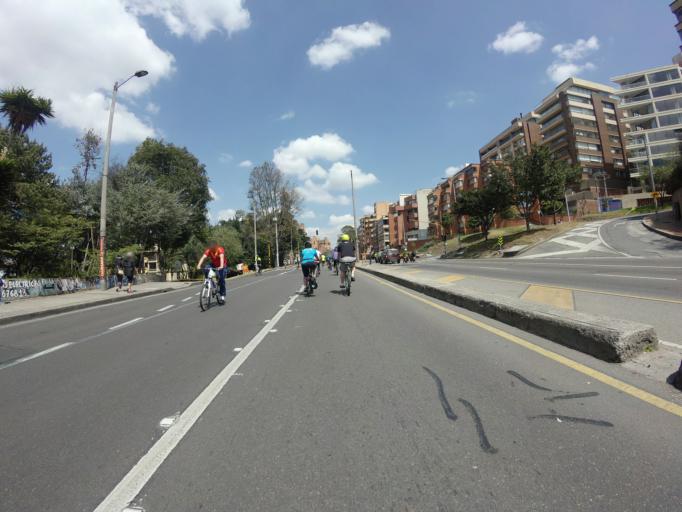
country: CO
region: Bogota D.C.
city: Barrio San Luis
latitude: 4.6710
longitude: -74.0441
